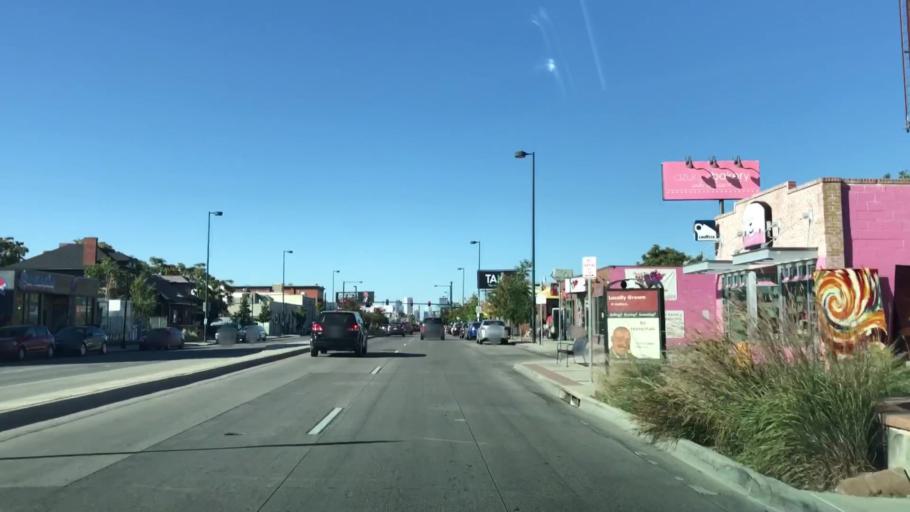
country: US
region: Colorado
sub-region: Arapahoe County
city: Englewood
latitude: 39.6822
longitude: -104.9876
